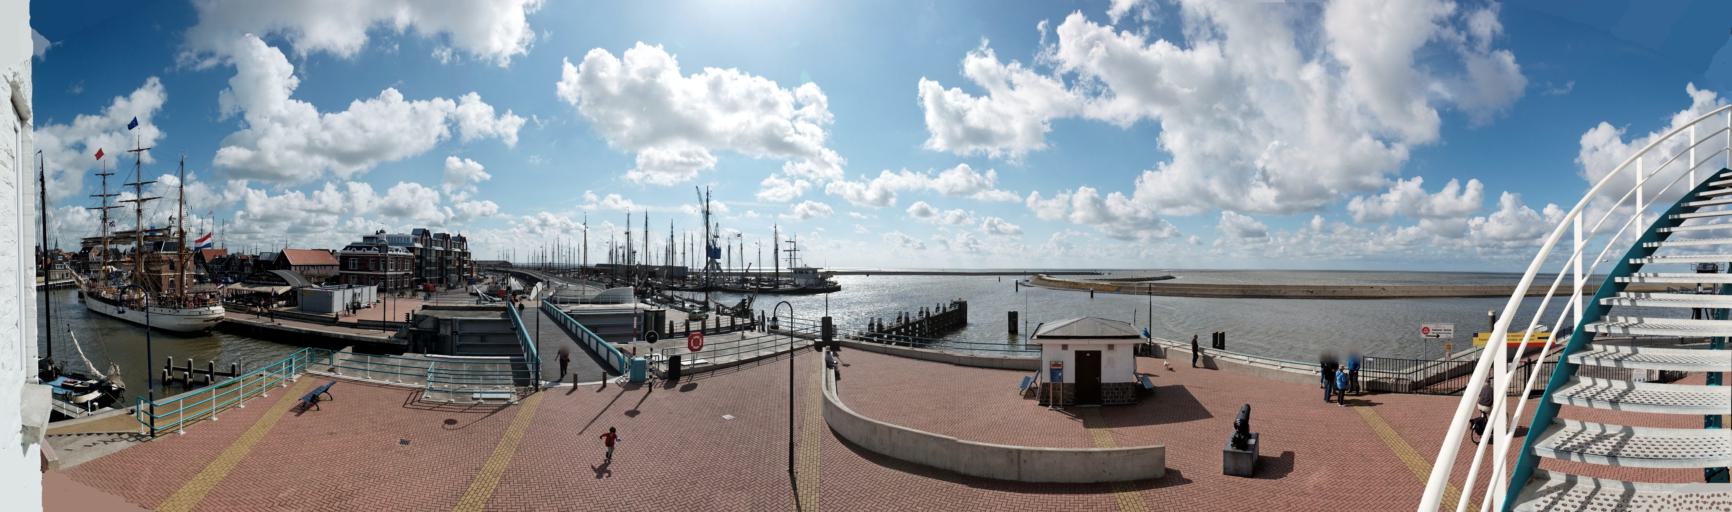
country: NL
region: Friesland
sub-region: Gemeente Harlingen
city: Harlingen
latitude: 53.1757
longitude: 5.4115
